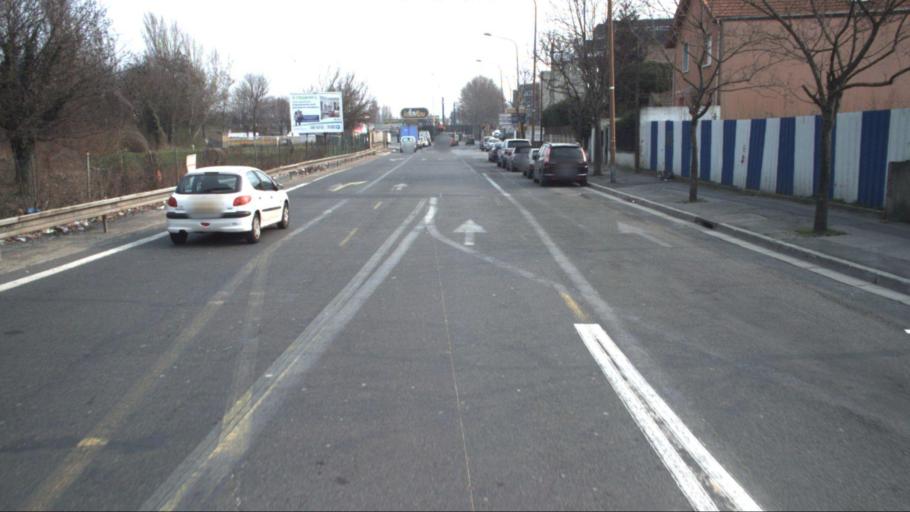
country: FR
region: Ile-de-France
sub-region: Departement du Val-d'Oise
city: Bezons
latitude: 48.9169
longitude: 2.2225
